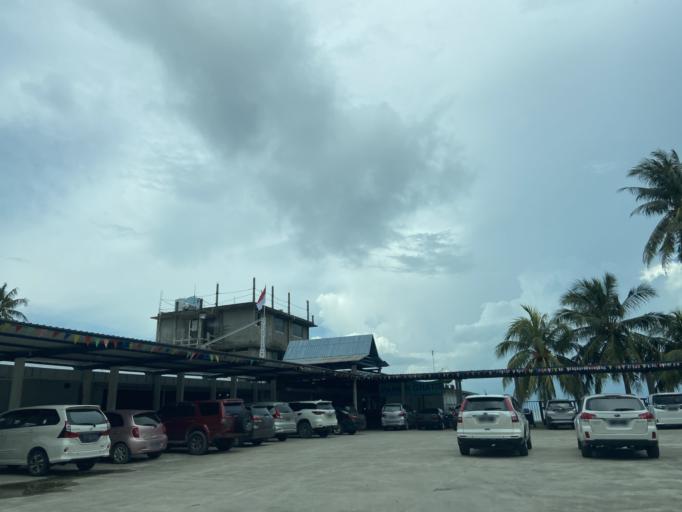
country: SG
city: Singapore
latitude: 1.1535
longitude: 104.1399
